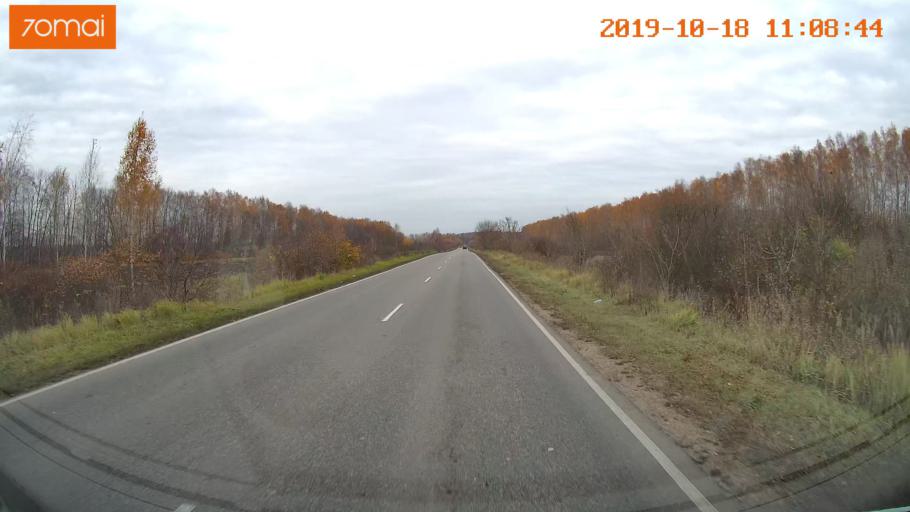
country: RU
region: Tula
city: Kimovsk
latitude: 53.9427
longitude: 38.5355
